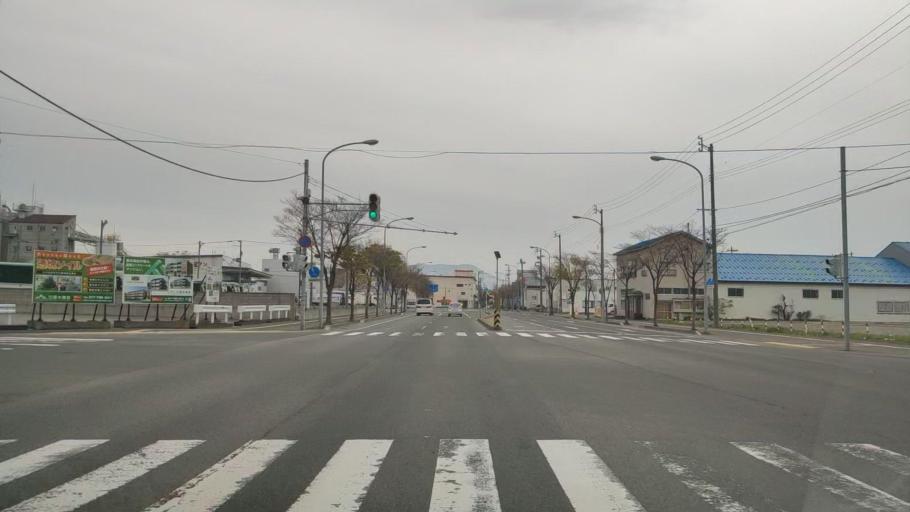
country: JP
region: Aomori
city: Aomori Shi
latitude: 40.8290
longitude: 140.7518
